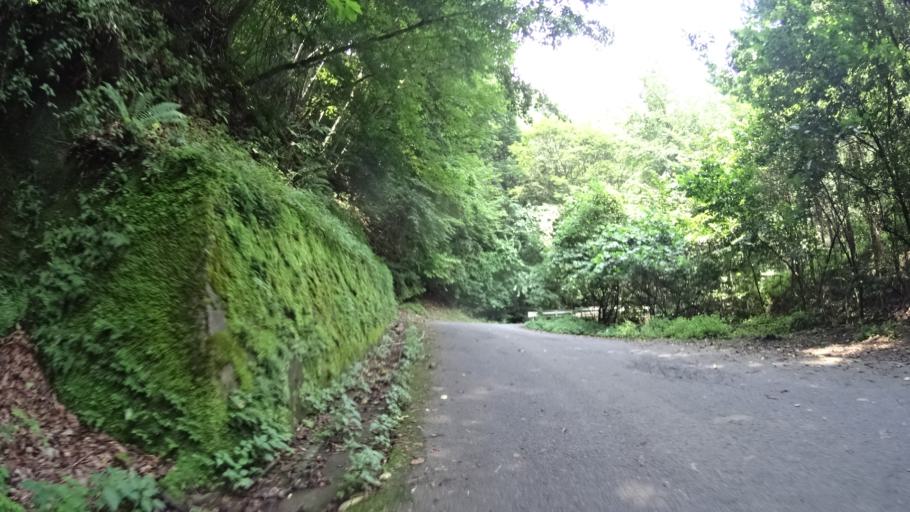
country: JP
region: Gunma
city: Tomioka
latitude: 36.0812
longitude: 138.7087
